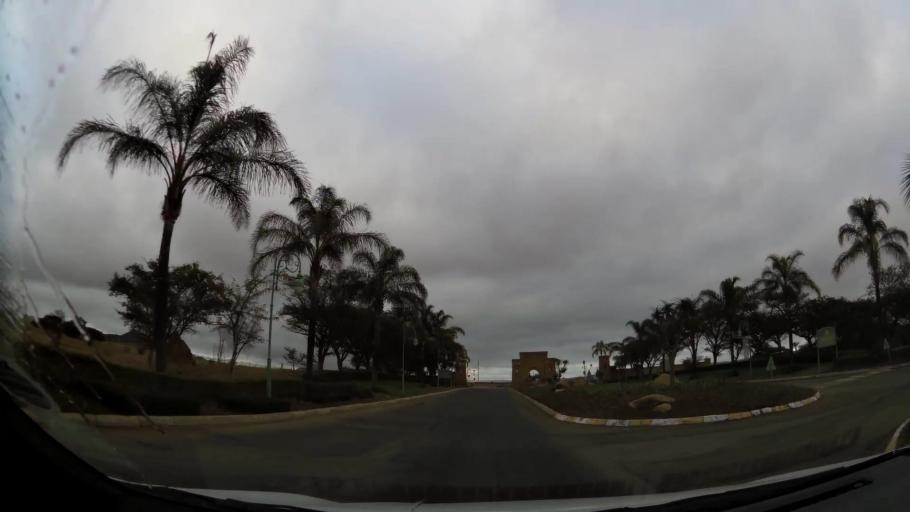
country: ZA
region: Limpopo
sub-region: Capricorn District Municipality
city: Polokwane
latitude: -23.9427
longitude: 29.4227
